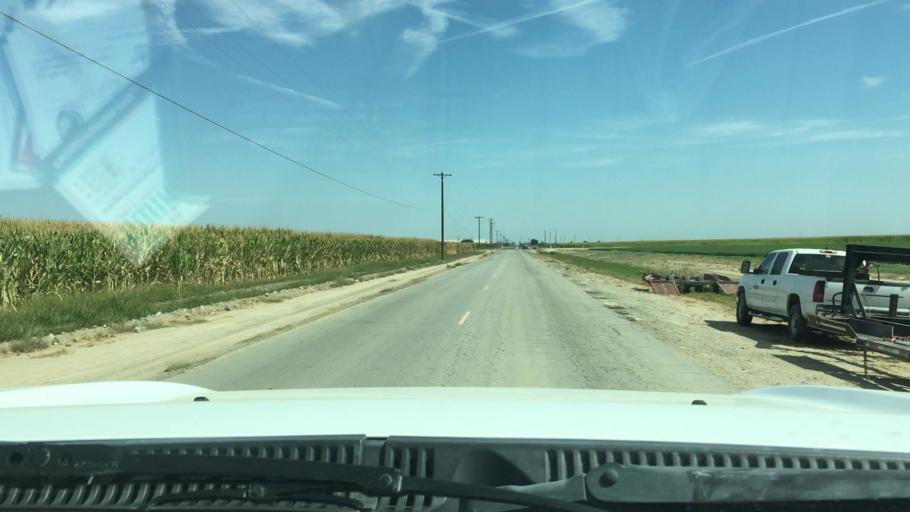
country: US
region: California
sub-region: Kern County
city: Buttonwillow
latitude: 35.4028
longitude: -119.3767
